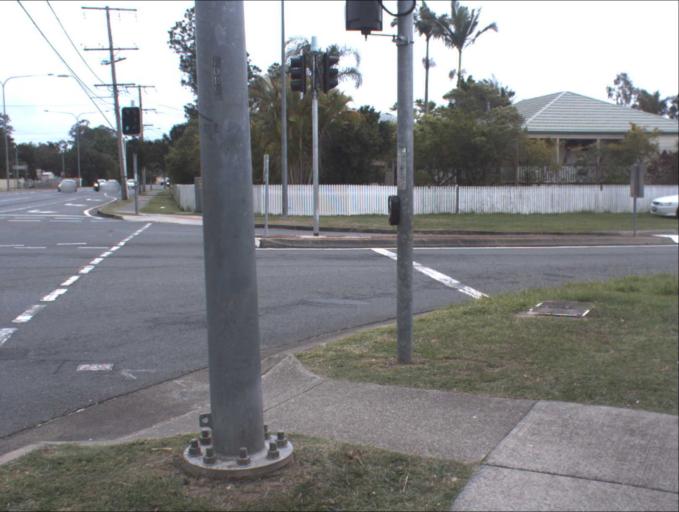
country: AU
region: Queensland
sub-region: Logan
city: Waterford West
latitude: -27.6909
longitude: 153.1286
